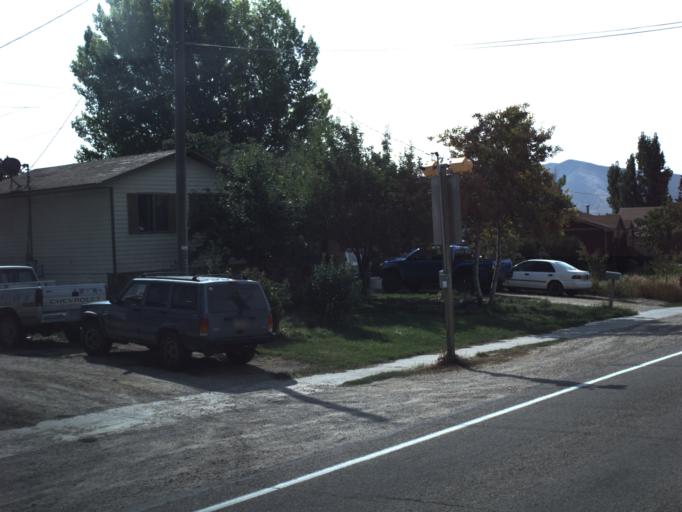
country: US
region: Utah
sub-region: Wasatch County
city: Midway
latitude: 40.5099
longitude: -111.4724
